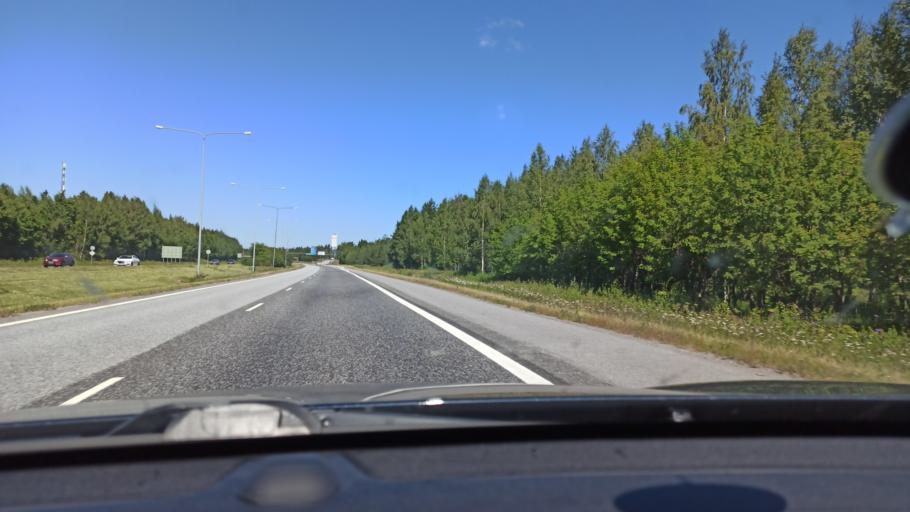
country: FI
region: Ostrobothnia
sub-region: Vaasa
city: Ristinummi
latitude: 63.0646
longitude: 21.7056
